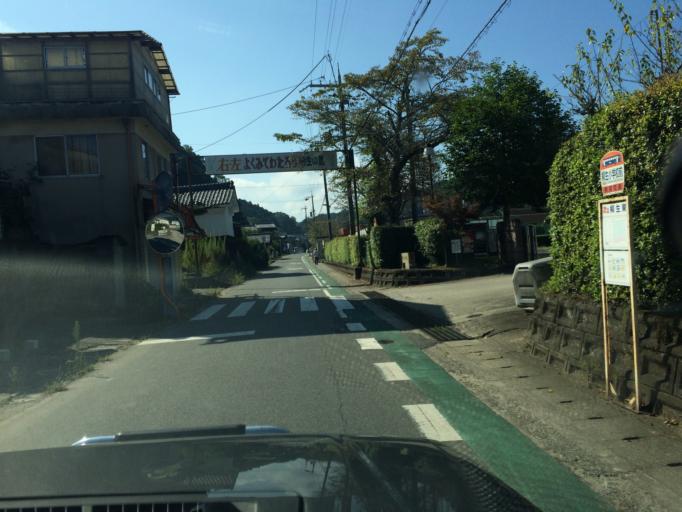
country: JP
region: Nara
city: Nara-shi
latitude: 34.7381
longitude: 135.9520
